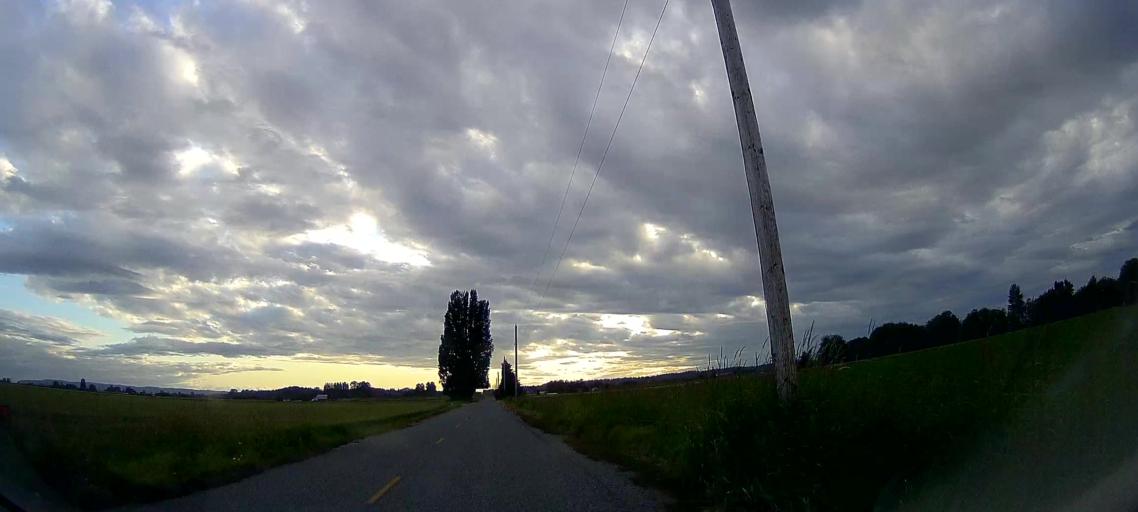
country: US
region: Washington
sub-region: Skagit County
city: Mount Vernon
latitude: 48.3702
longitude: -122.3845
